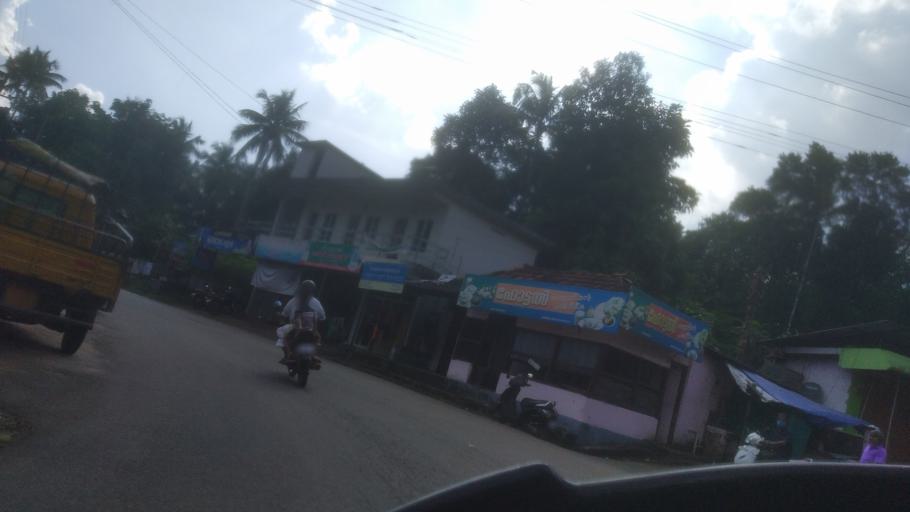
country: IN
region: Kerala
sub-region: Ernakulam
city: Kotamangalam
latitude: 10.0007
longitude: 76.6459
